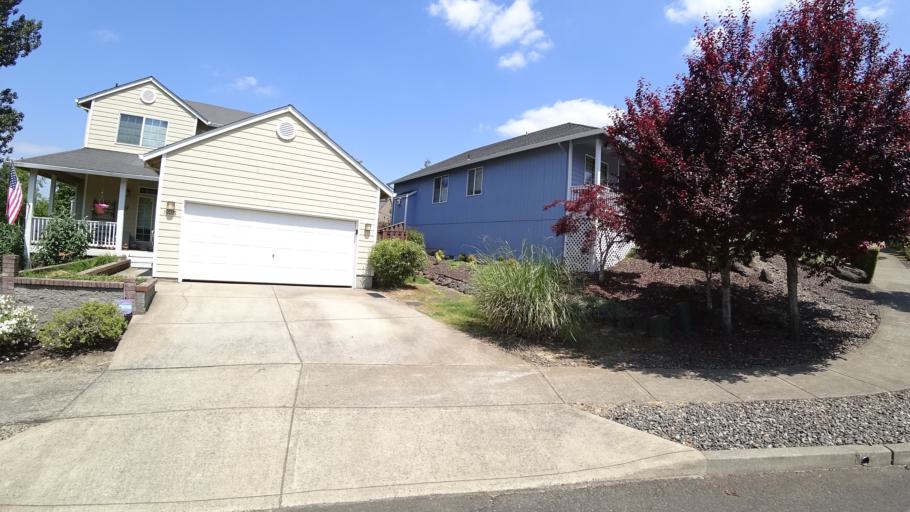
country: US
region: Oregon
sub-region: Clackamas County
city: Happy Valley
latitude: 45.4735
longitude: -122.5085
